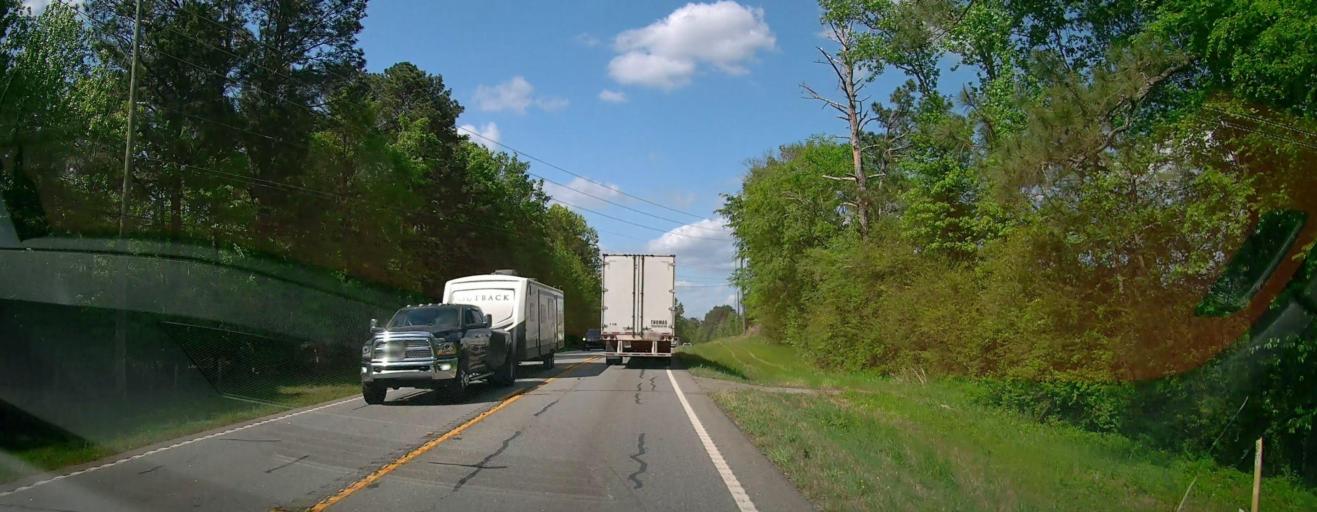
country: US
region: Georgia
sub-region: Greene County
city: Greensboro
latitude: 33.5226
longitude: -83.2222
